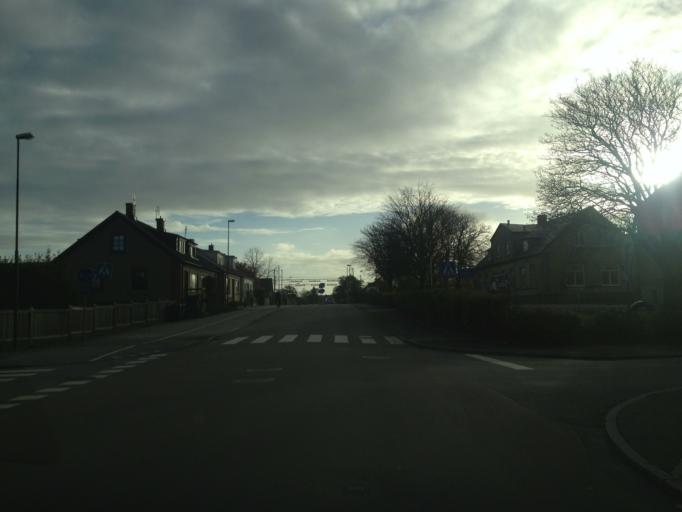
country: SE
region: Skane
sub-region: Lomma Kommun
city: Lomma
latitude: 55.6750
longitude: 13.0730
